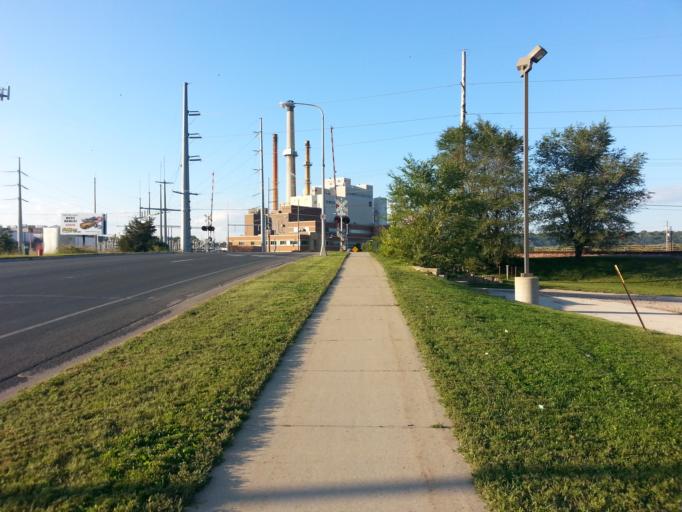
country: US
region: Minnesota
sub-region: Olmsted County
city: Rochester
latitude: 44.0258
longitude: -92.4600
